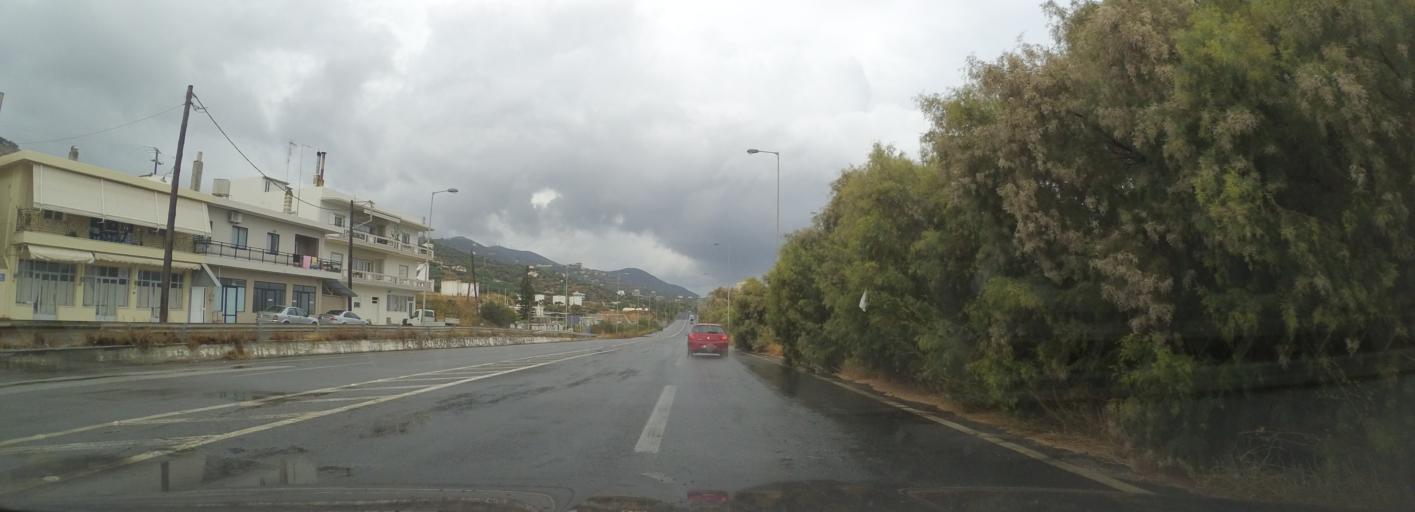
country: GR
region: Crete
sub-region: Nomos Irakleiou
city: Gazi
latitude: 35.3422
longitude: 25.0480
